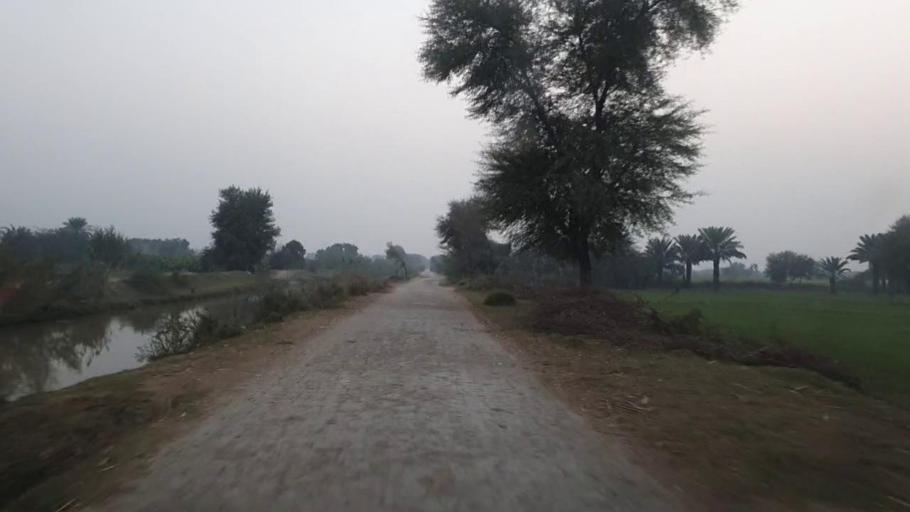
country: PK
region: Sindh
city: Karaundi
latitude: 26.9368
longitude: 68.4432
